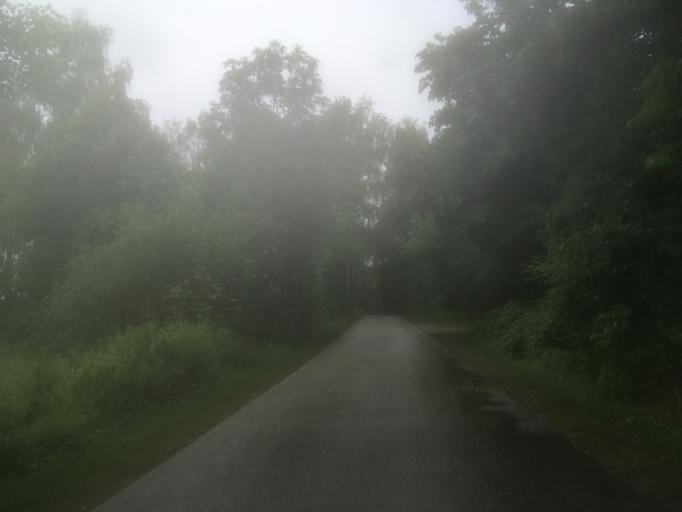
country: DE
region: Brandenburg
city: Zehdenick
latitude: 53.0380
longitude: 13.3075
